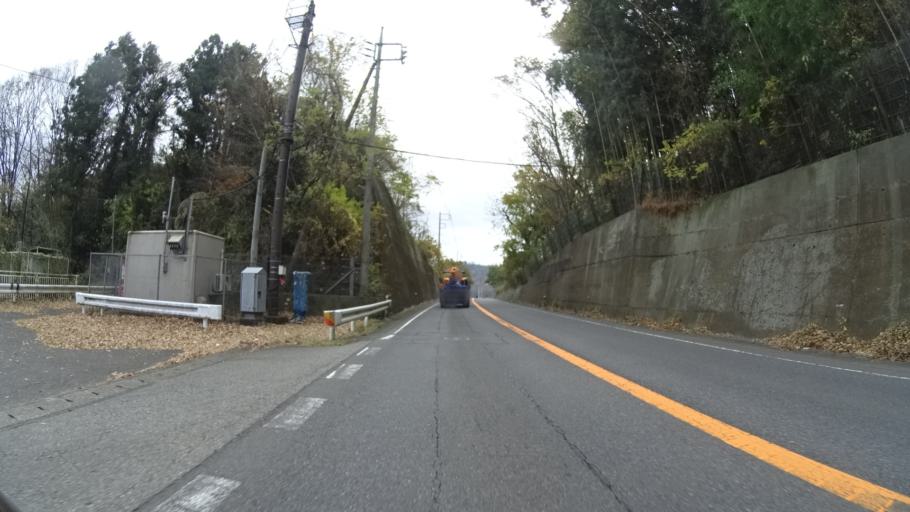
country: JP
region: Gunma
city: Numata
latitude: 36.5753
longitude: 139.0495
